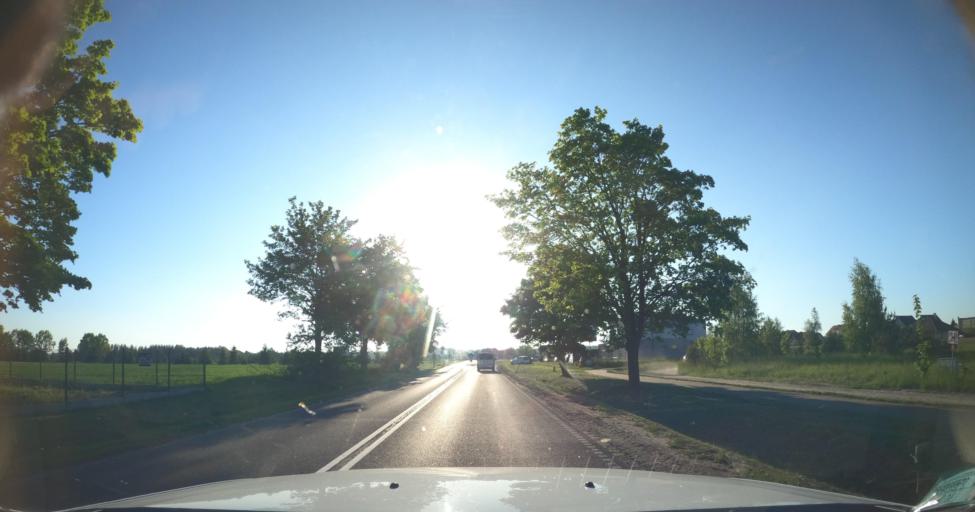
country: PL
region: Pomeranian Voivodeship
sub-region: Powiat kartuski
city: Kartuzy
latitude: 54.3177
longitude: 18.2605
